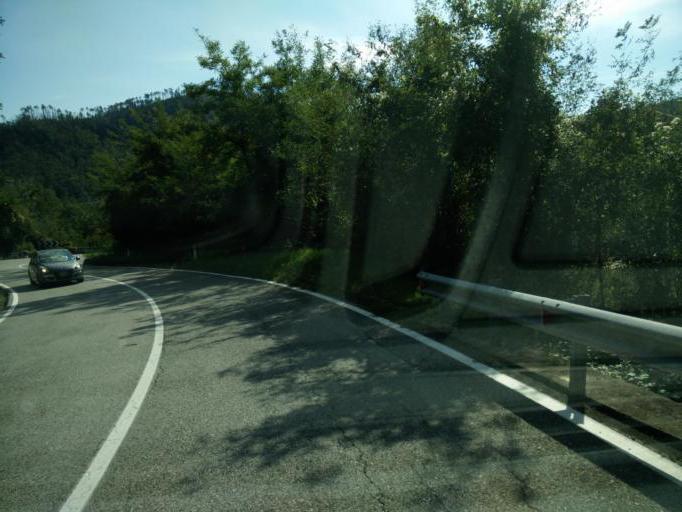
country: IT
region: Liguria
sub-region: Provincia di La Spezia
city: Carrodano
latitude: 44.2420
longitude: 9.6601
